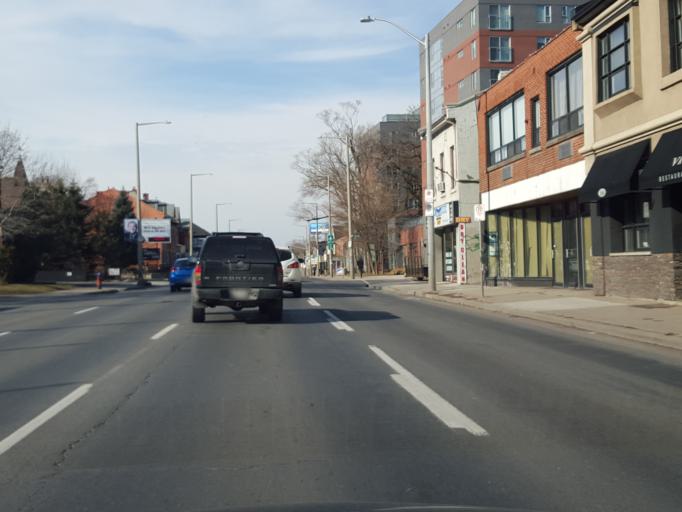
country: CA
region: Ontario
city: Hamilton
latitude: 43.2597
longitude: -79.8799
